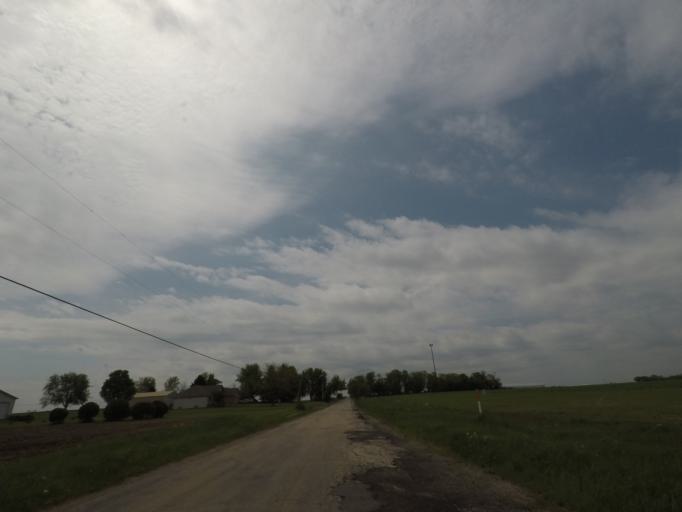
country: US
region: Illinois
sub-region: Winnebago County
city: Machesney Park
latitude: 42.3429
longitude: -88.9494
